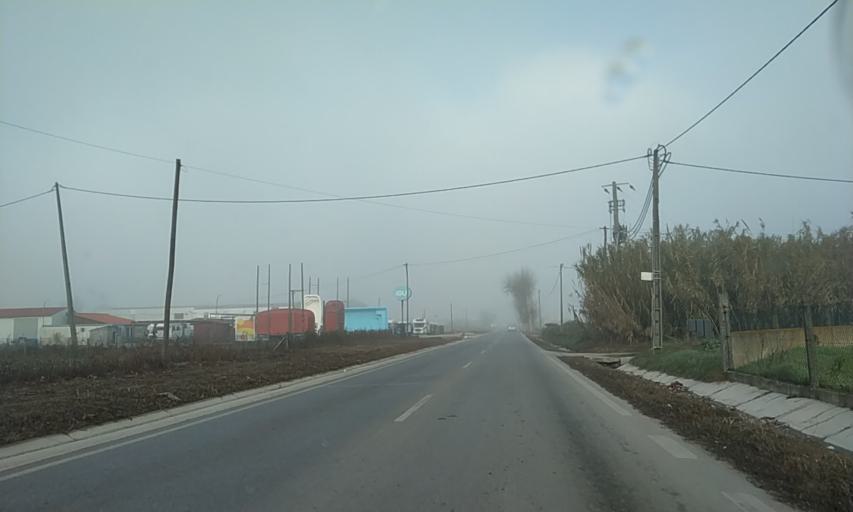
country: PT
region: Setubal
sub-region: Palmela
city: Pinhal Novo
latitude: 38.6594
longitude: -8.9218
